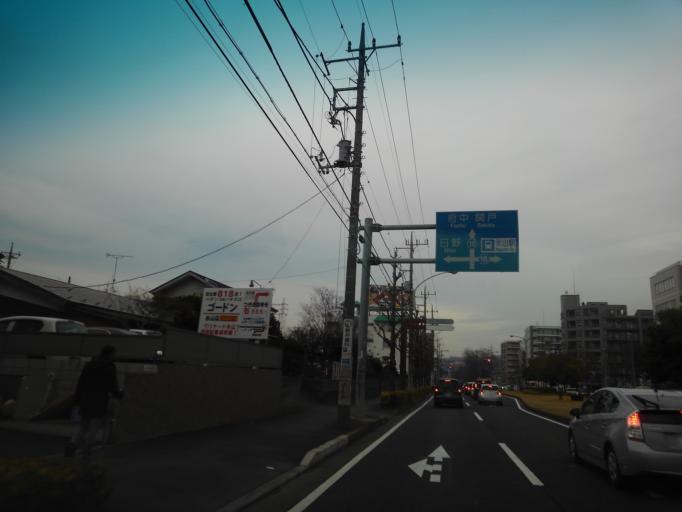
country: JP
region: Tokyo
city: Hino
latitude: 35.6342
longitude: 139.4450
